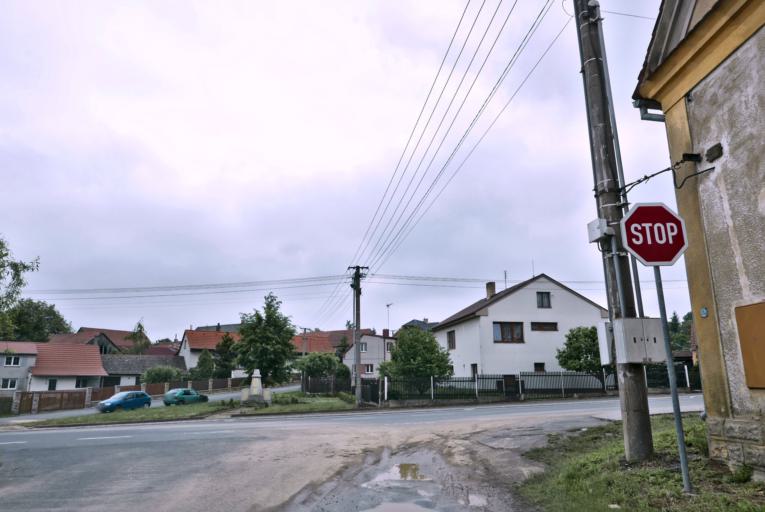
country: CZ
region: Plzensky
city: Kralovice
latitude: 49.9653
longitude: 13.4516
